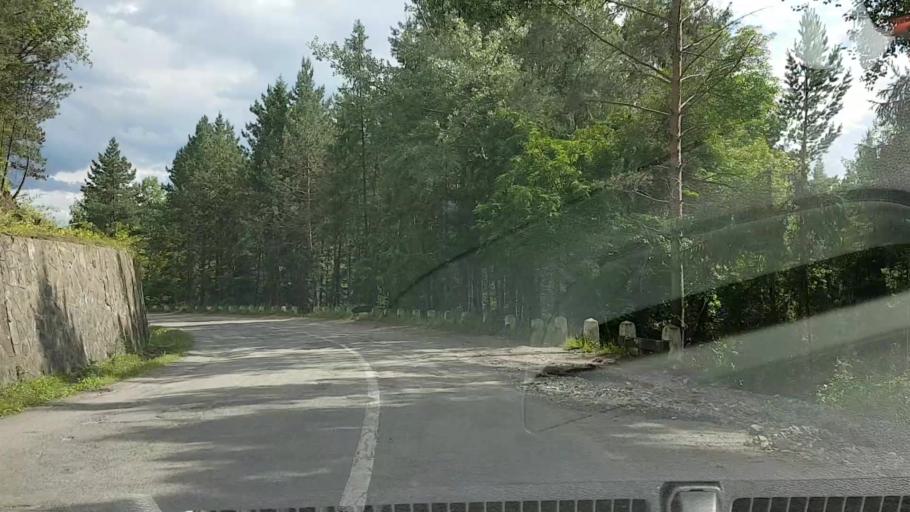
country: RO
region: Neamt
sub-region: Comuna Hangu
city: Hangu
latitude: 47.0501
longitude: 26.0083
